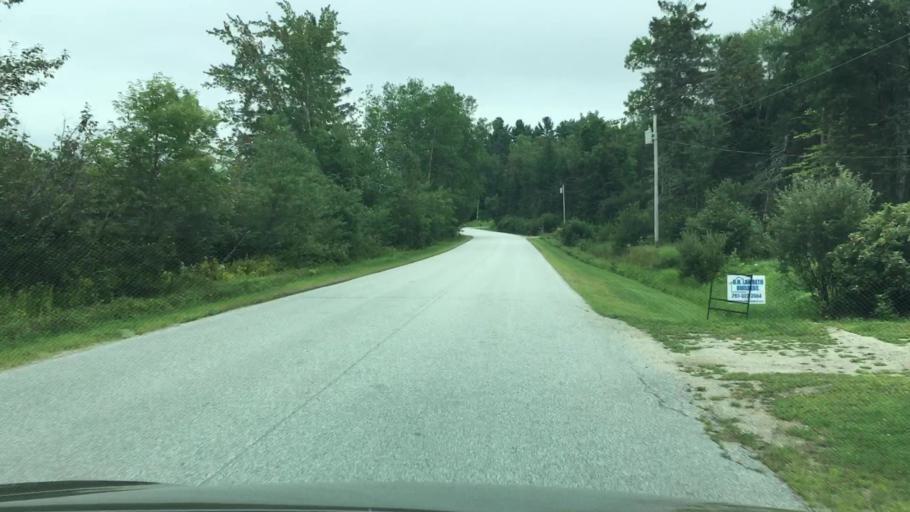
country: US
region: Maine
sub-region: Waldo County
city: Stockton Springs
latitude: 44.5273
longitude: -68.8274
